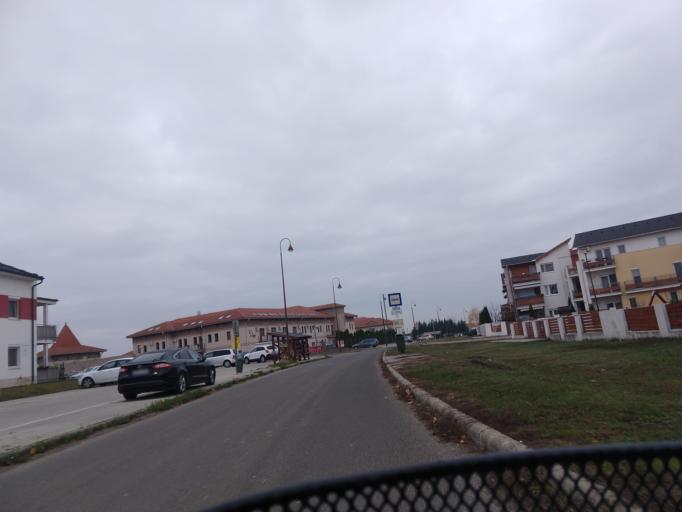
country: HU
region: Pest
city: Orbottyan
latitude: 47.6581
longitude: 19.2575
